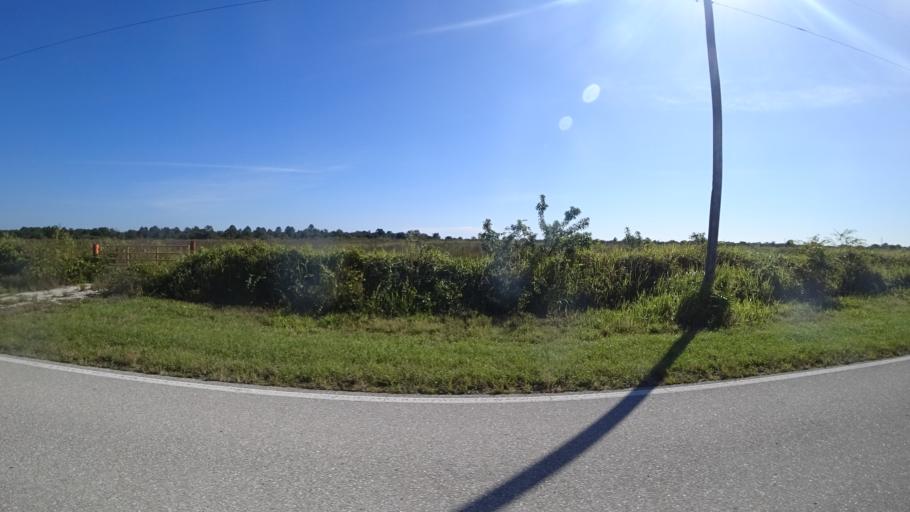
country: US
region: Florida
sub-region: Hillsborough County
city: Wimauma
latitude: 27.6101
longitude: -82.2927
